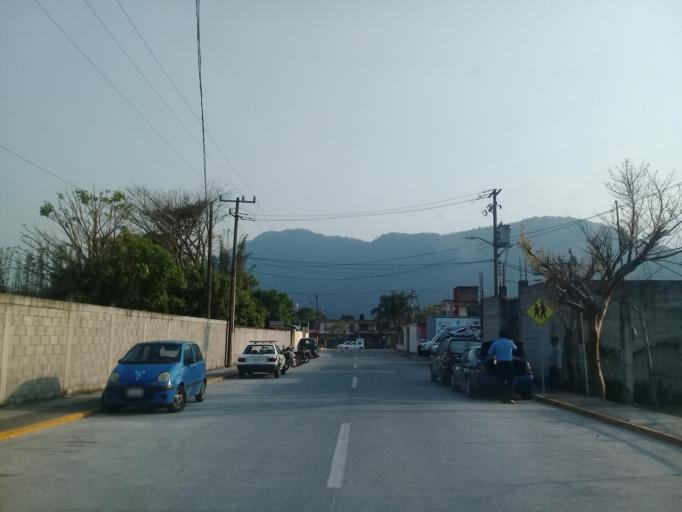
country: MX
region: Veracruz
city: Ixtac Zoquitlan
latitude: 18.8527
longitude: -97.0529
